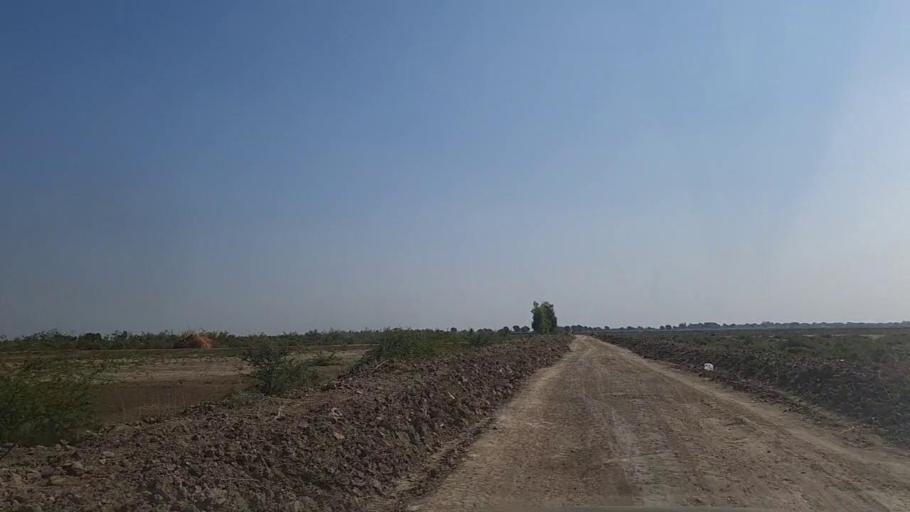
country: PK
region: Sindh
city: Digri
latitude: 25.1632
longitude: 69.1720
